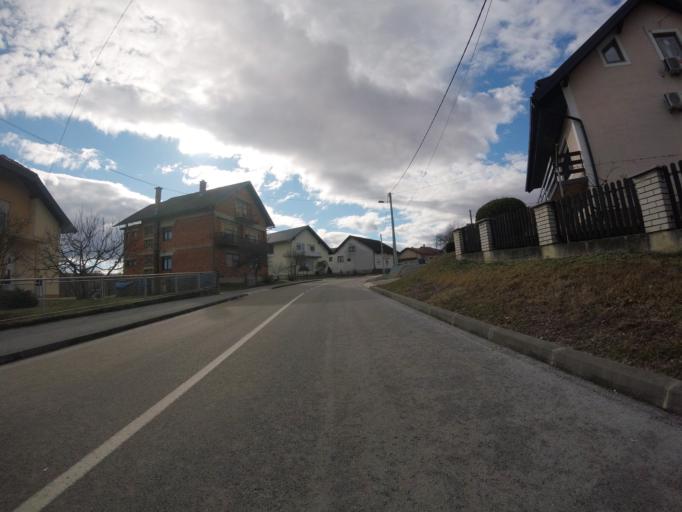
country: HR
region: Zagrebacka
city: Mraclin
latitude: 45.6346
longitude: 16.0568
